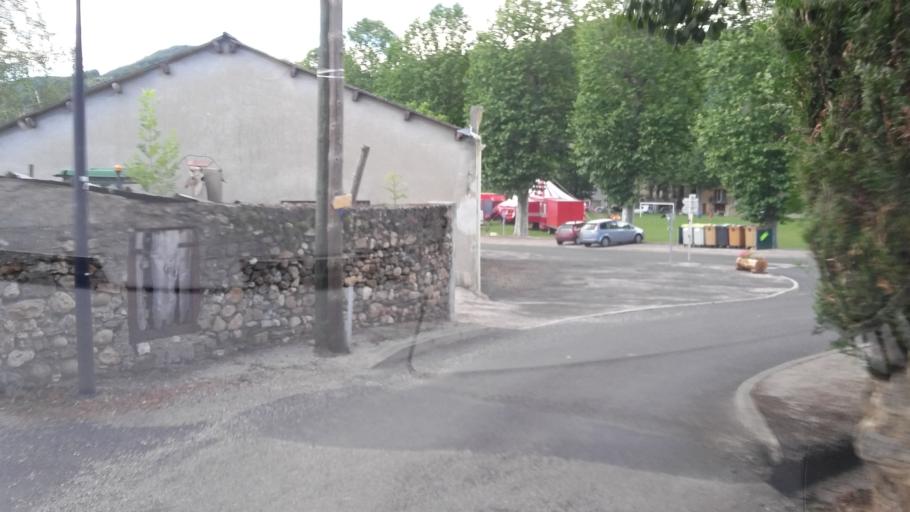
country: FR
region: Languedoc-Roussillon
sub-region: Departement de la Lozere
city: Meyrueis
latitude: 44.0203
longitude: 3.3620
